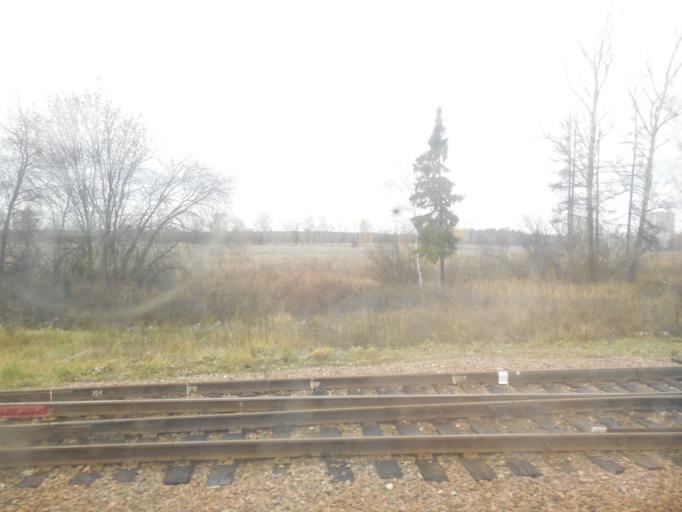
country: RU
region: Moskovskaya
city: Zvenigorod
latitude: 55.6968
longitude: 36.8715
